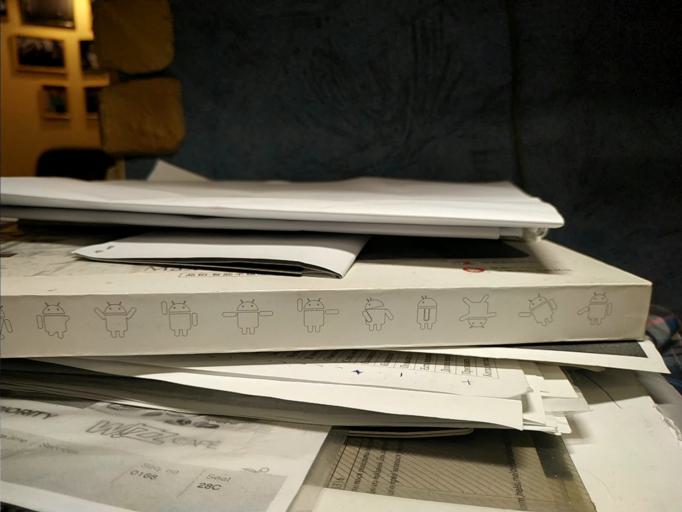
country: RU
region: Tverskaya
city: Zubtsov
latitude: 56.0808
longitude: 34.7989
